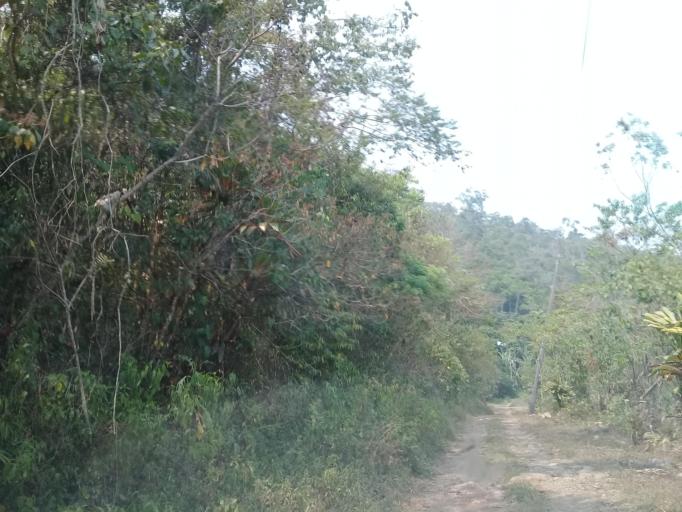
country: MX
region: Veracruz
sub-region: Tezonapa
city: Laguna Chica (Pueblo Nuevo)
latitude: 18.5834
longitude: -96.7497
